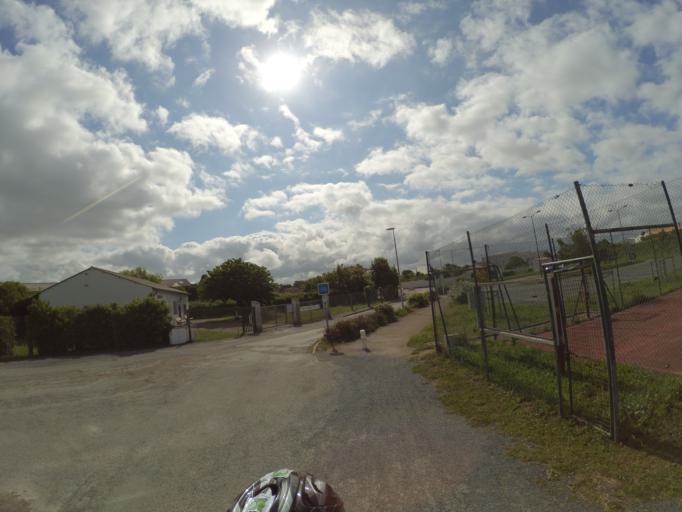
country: FR
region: Poitou-Charentes
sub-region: Departement de la Charente-Maritime
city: Angoulins
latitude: 46.1081
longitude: -1.1166
